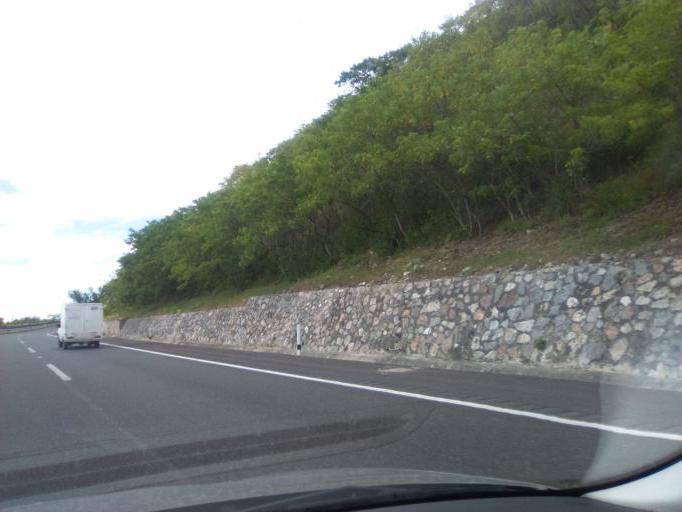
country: MX
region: Guerrero
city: Zumpango del Rio
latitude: 17.6860
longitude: -99.5000
